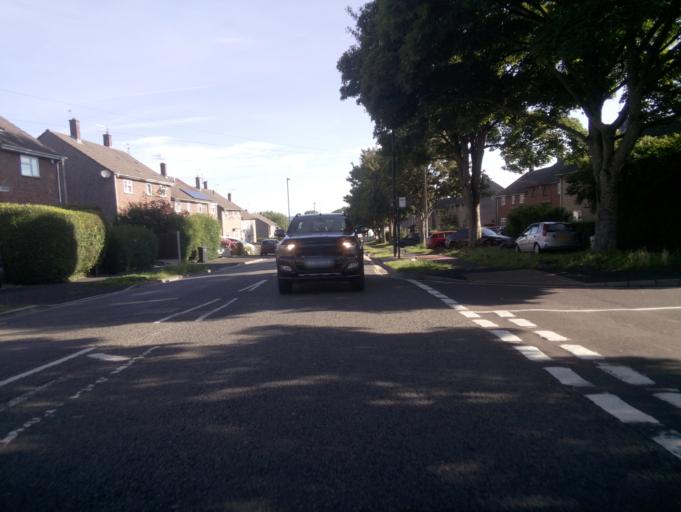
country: GB
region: England
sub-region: Bath and North East Somerset
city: Whitchurch
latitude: 51.4122
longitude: -2.5537
